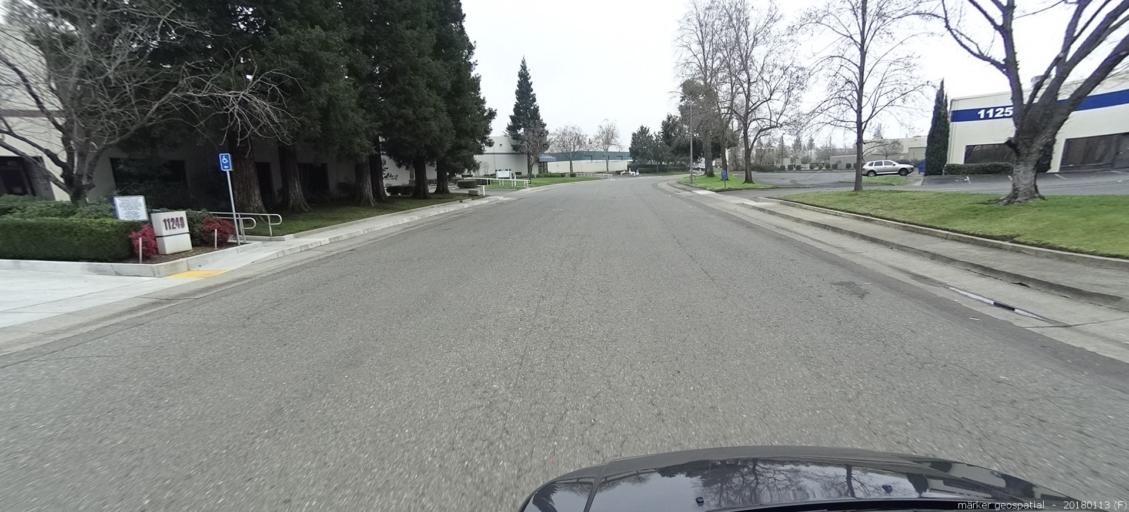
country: US
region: California
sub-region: Sacramento County
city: Gold River
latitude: 38.6046
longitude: -121.2645
